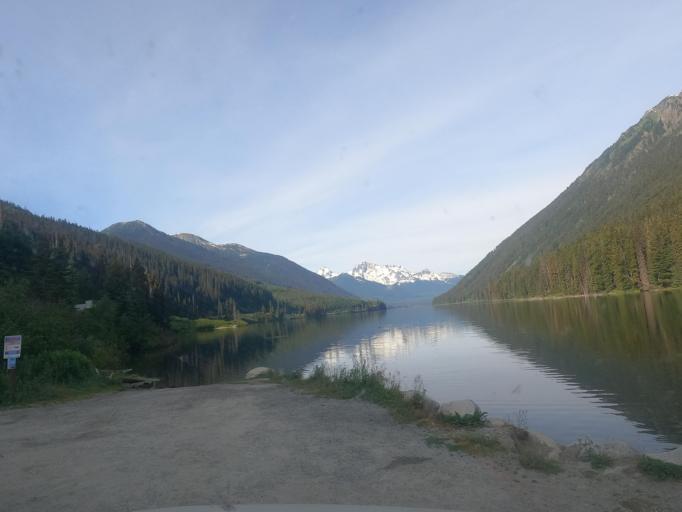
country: CA
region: British Columbia
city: Lillooet
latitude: 50.4189
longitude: -122.2788
